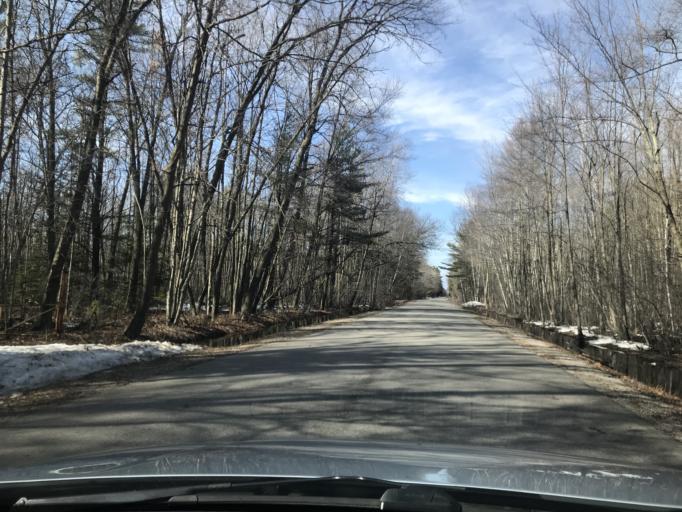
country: US
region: Wisconsin
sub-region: Marinette County
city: Marinette
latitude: 45.0247
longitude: -87.6674
